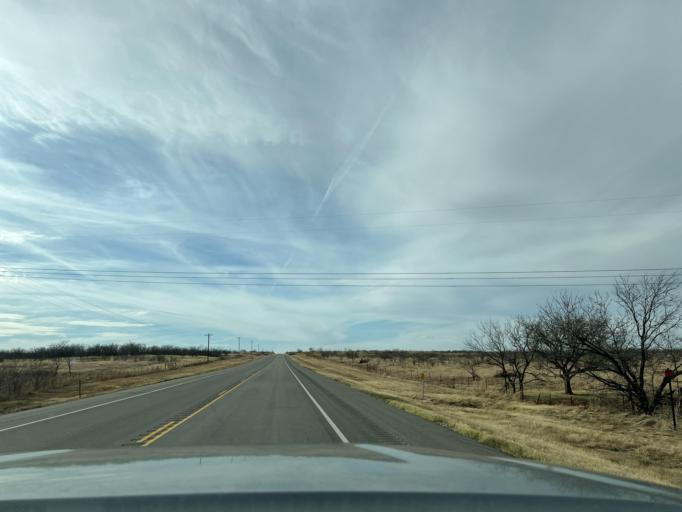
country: US
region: Texas
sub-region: Jones County
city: Anson
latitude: 32.7508
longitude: -99.7324
